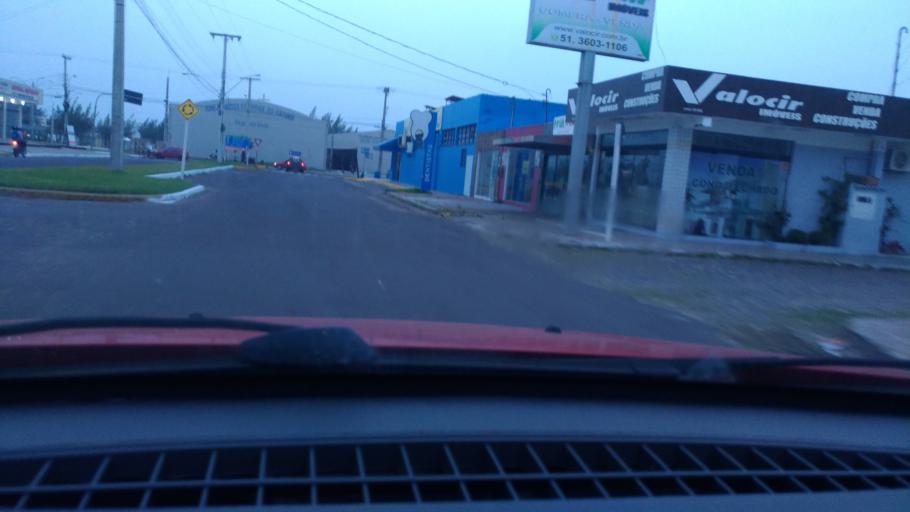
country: BR
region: Rio Grande do Sul
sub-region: Capao Da Canoa
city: Capao da Canoa
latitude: -29.8529
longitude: -50.0666
